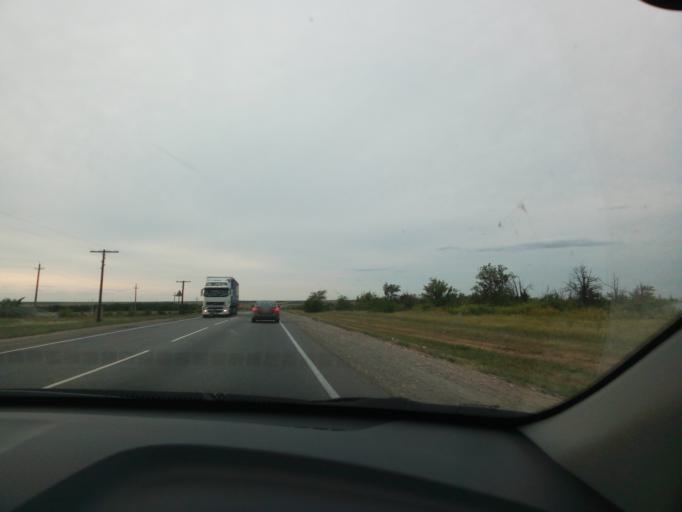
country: RU
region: Volgograd
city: Dubovka
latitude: 49.1123
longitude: 44.8110
